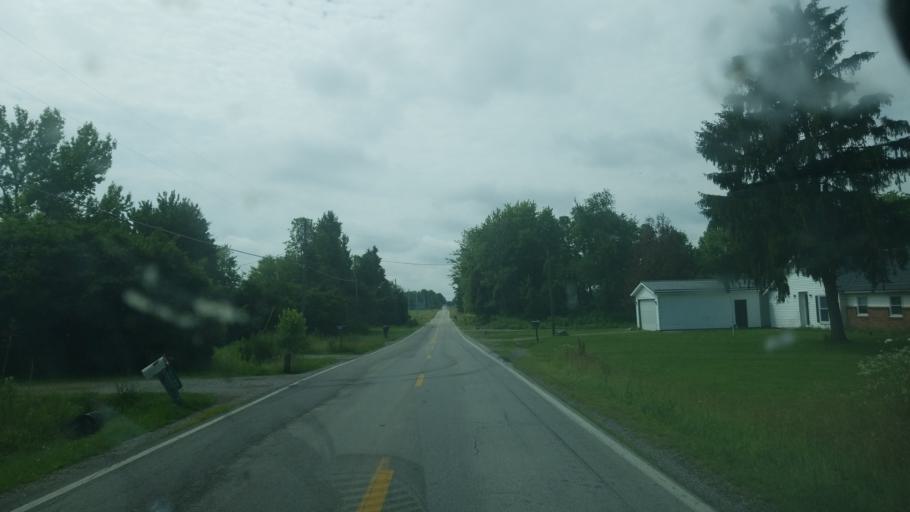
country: US
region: Ohio
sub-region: Licking County
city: Johnstown
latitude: 40.1505
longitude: -82.7600
